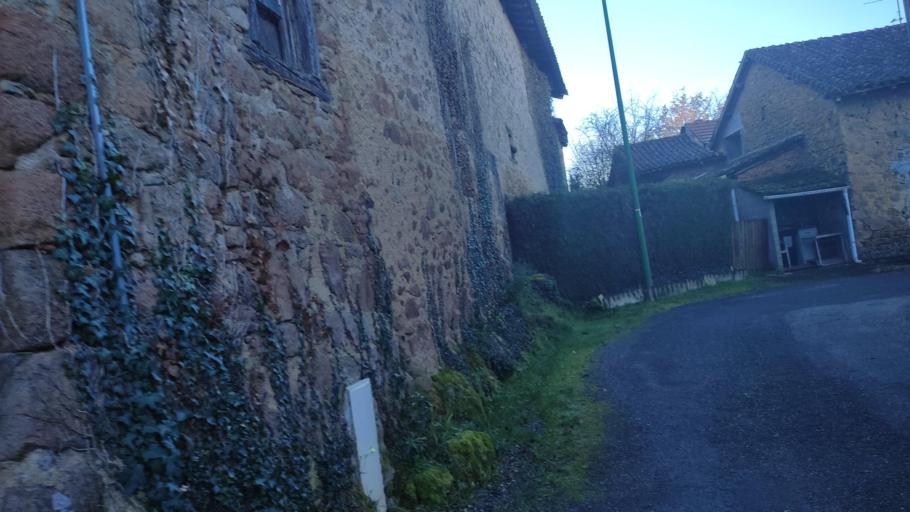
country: FR
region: Limousin
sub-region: Departement de la Haute-Vienne
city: Bosmie-l'Aiguille
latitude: 45.7652
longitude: 1.2174
